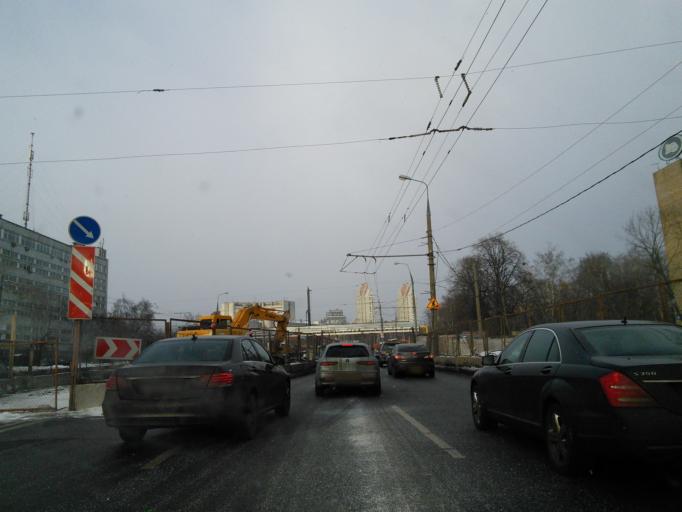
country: RU
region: Moskovskaya
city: Khoroshevo-Mnevniki
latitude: 55.7853
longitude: 37.4825
